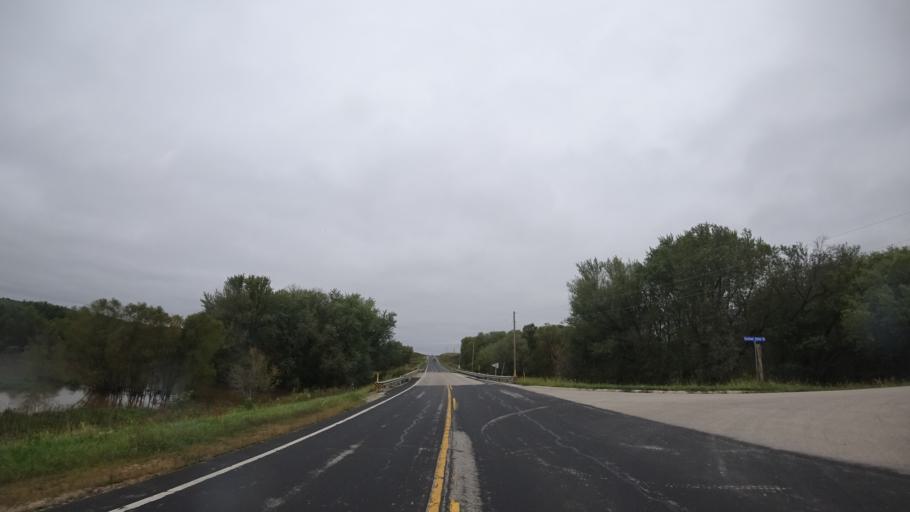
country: US
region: Wisconsin
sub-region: Grant County
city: Boscobel
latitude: 43.1105
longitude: -90.8039
